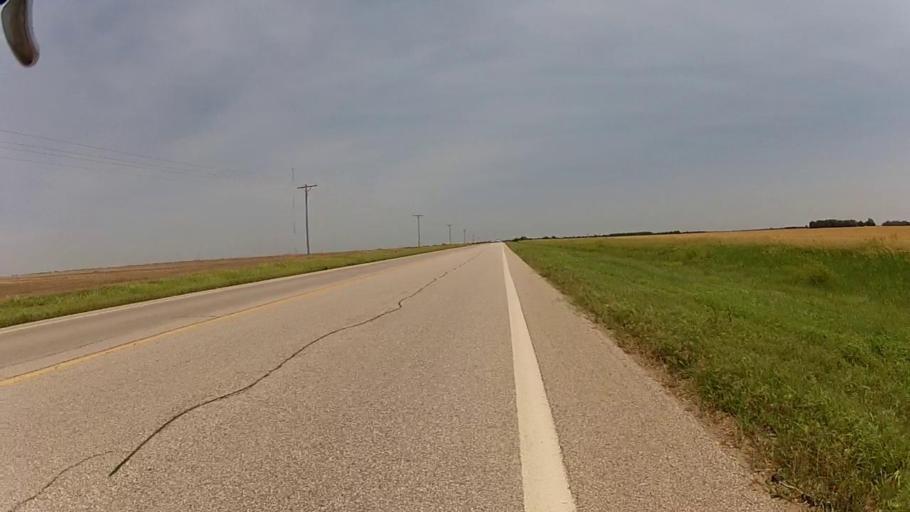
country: US
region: Kansas
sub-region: Cowley County
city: Arkansas City
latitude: 37.0565
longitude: -97.1027
